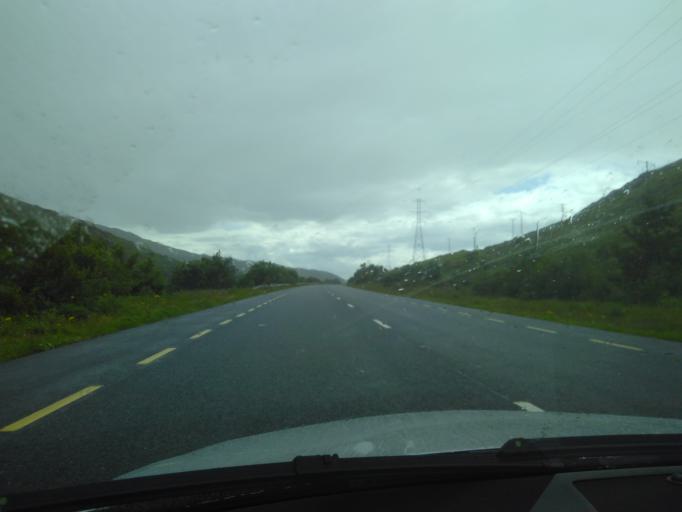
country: IE
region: Ulster
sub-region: County Donegal
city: Donegal
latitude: 54.7156
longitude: -7.9615
